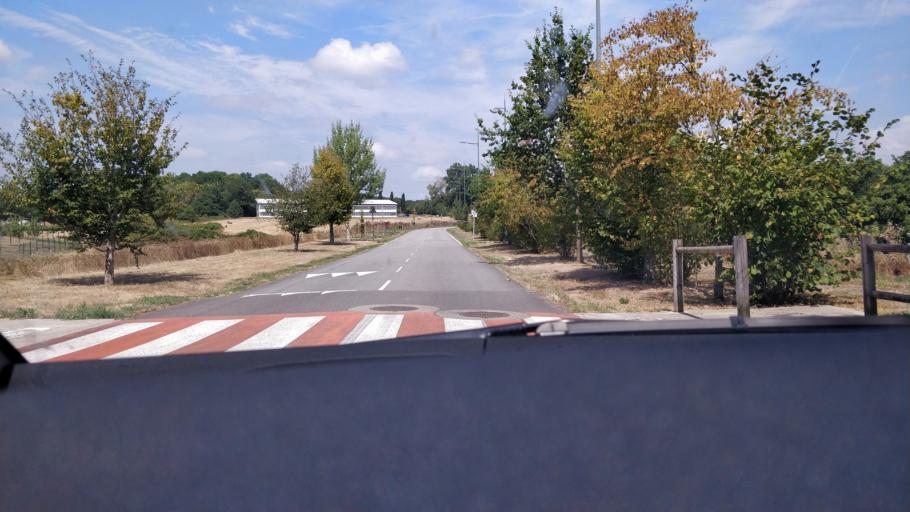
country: FR
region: Limousin
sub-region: Departement de la Haute-Vienne
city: Le Palais-sur-Vienne
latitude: 45.8589
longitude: 1.2990
